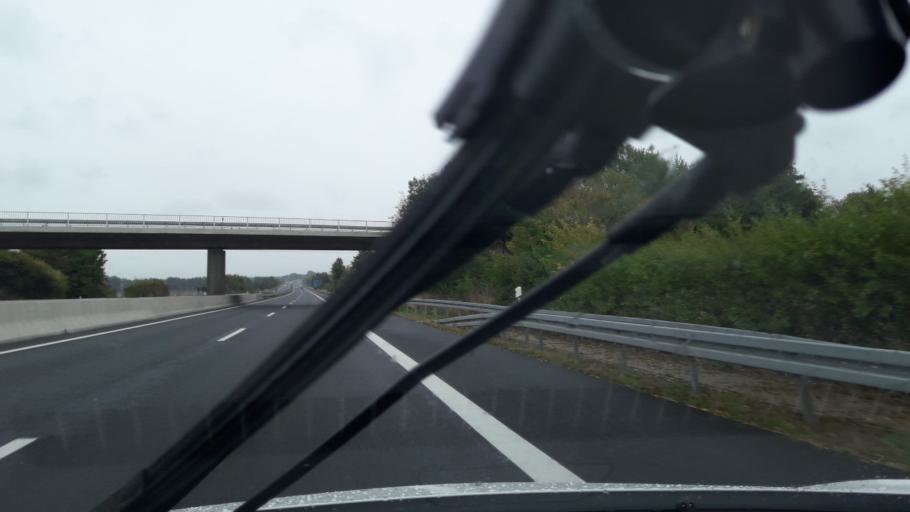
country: DE
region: Lower Saxony
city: Schladen
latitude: 52.0164
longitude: 10.5310
